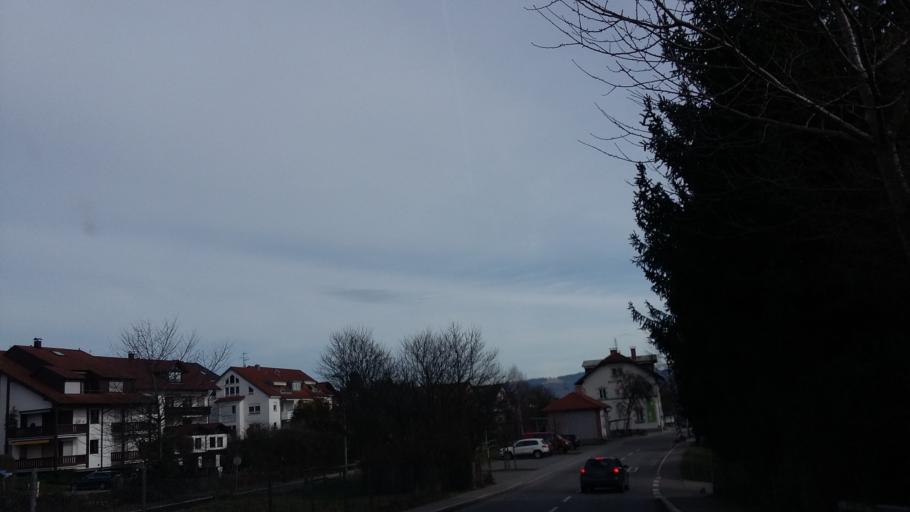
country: DE
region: Bavaria
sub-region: Swabia
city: Nonnenhorn
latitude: 47.5721
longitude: 9.6371
